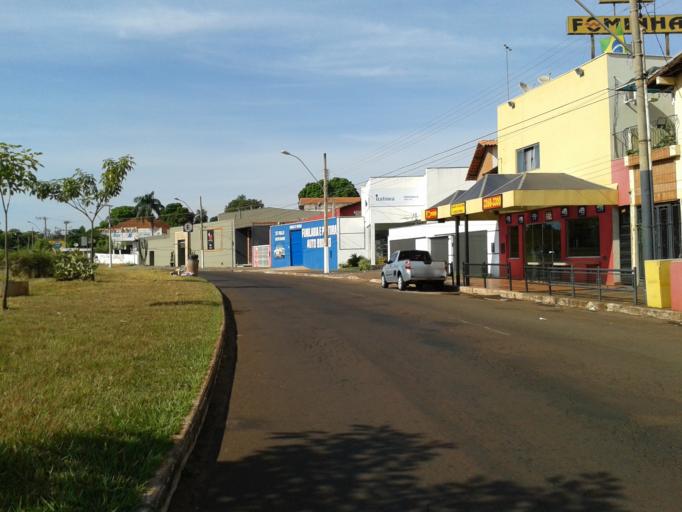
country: BR
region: Minas Gerais
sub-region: Ituiutaba
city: Ituiutaba
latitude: -18.9674
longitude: -49.4607
